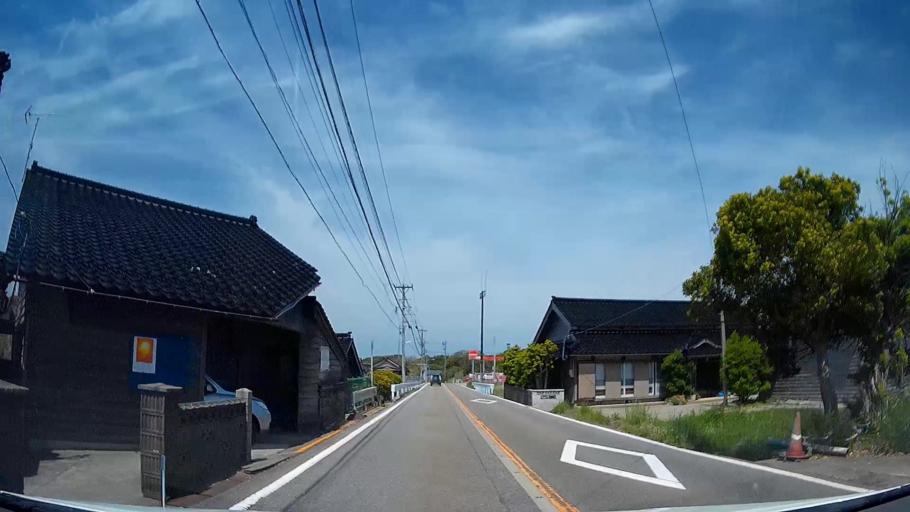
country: JP
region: Ishikawa
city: Hakui
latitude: 36.9428
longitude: 136.7625
